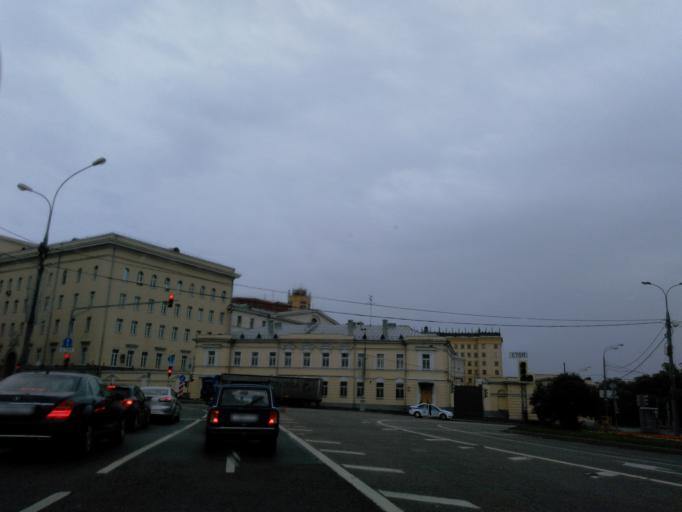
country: RU
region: Moscow
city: Moscow
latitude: 55.7516
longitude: 37.6013
